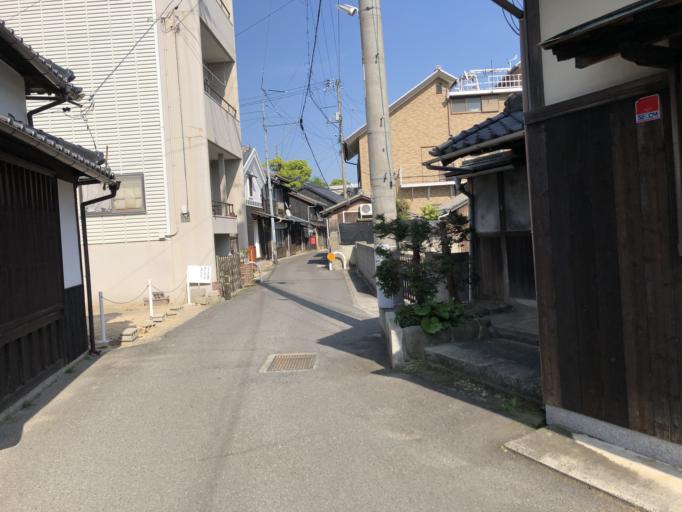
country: JP
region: Kagawa
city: Tonosho
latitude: 34.6141
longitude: 134.1684
